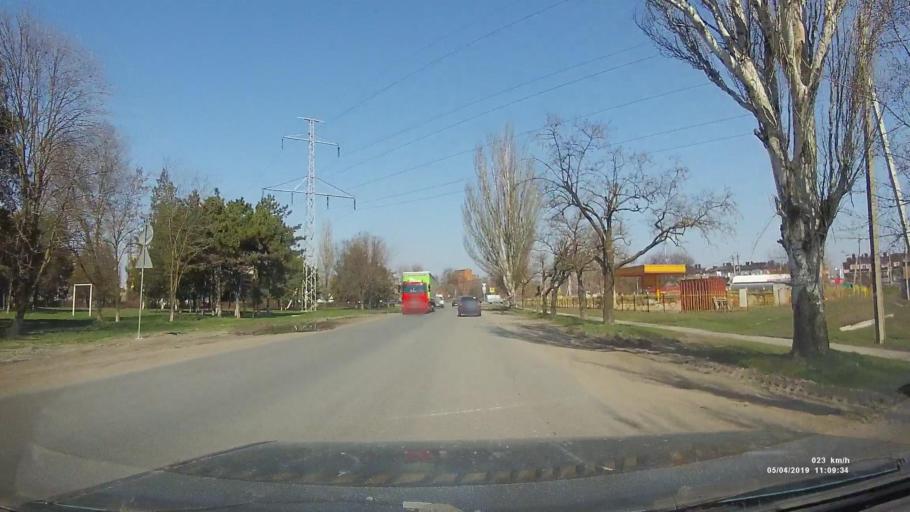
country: RU
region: Rostov
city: Azov
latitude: 47.0906
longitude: 39.4327
